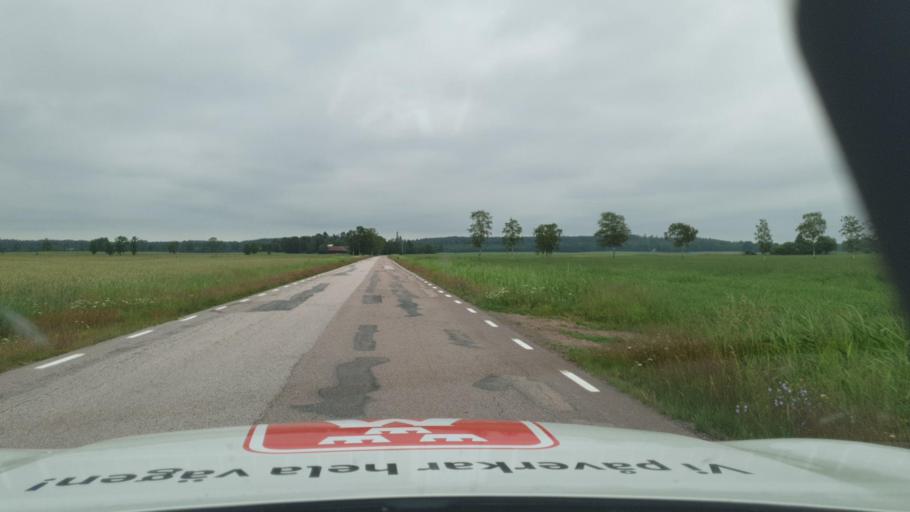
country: SE
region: Vaermland
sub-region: Karlstads Kommun
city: Skattkarr
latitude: 59.4023
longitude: 13.8643
